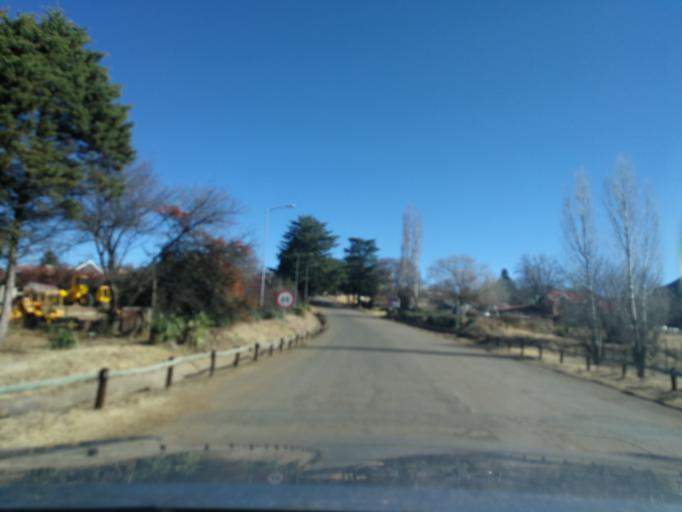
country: ZA
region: Orange Free State
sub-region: Thabo Mofutsanyana District Municipality
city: Bethlehem
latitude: -28.5113
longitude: 28.4242
